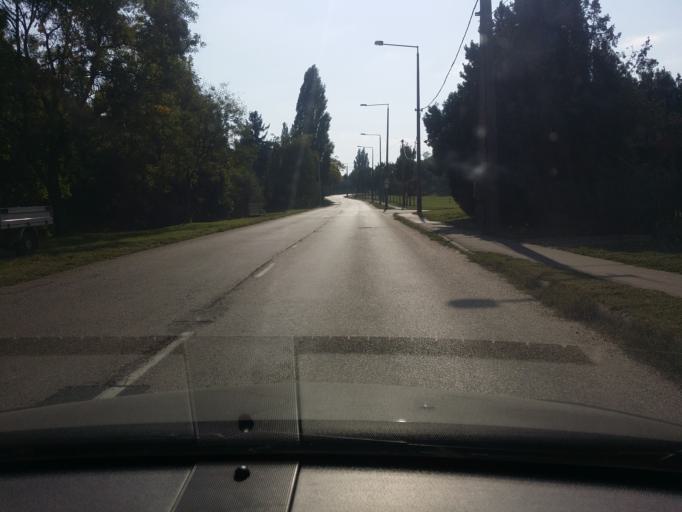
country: HU
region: Fejer
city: dunaujvaros
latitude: 46.9674
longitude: 18.9247
